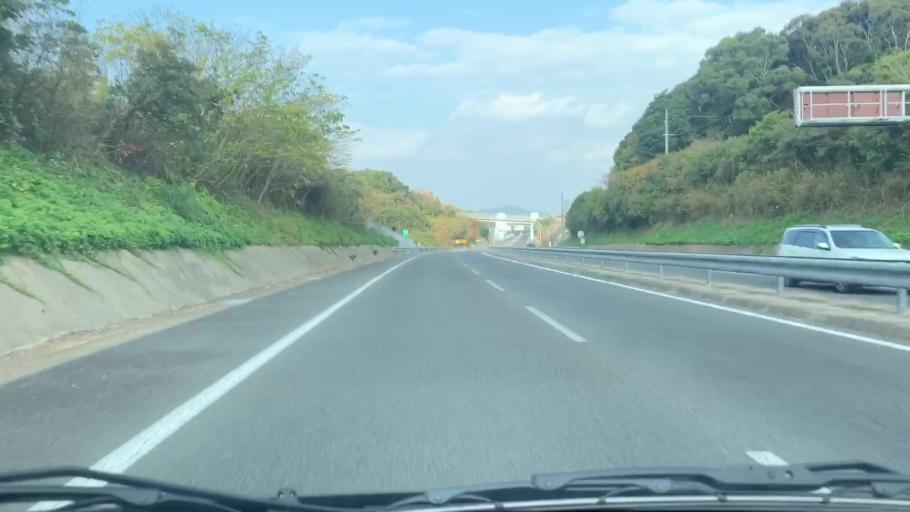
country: JP
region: Nagasaki
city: Sasebo
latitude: 33.0489
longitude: 129.7515
